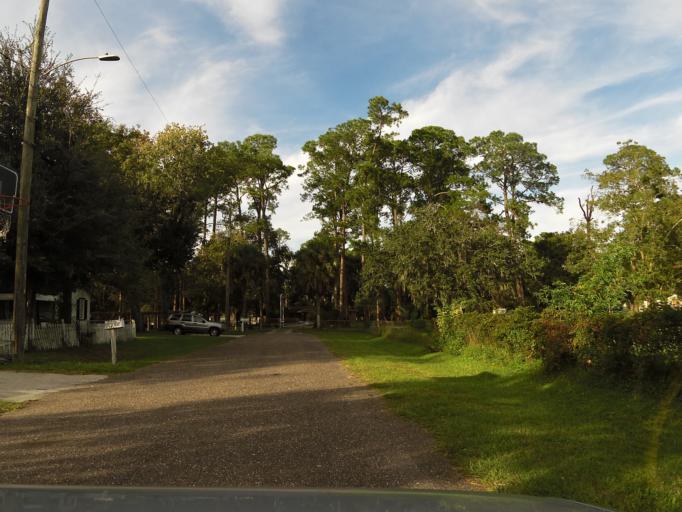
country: US
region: Florida
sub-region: Duval County
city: Jacksonville
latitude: 30.4119
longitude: -81.6536
